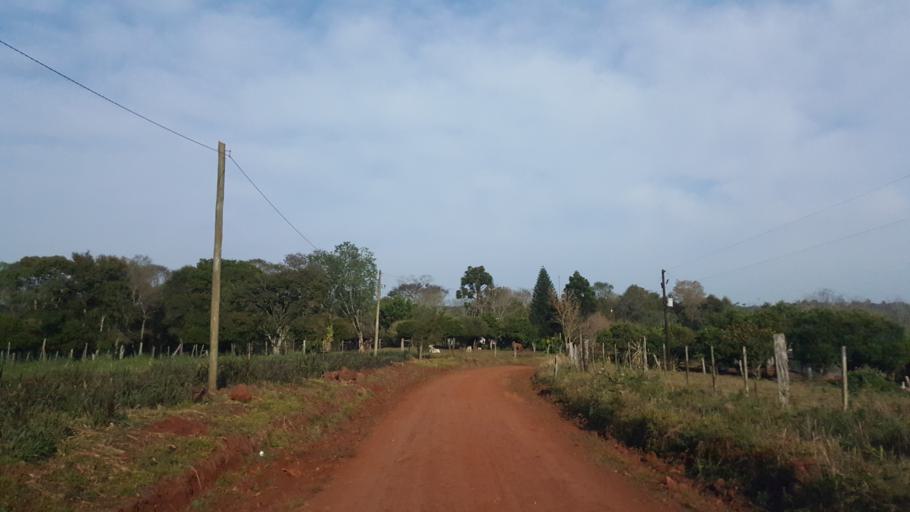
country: AR
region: Misiones
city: Capiovi
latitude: -26.9154
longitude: -55.0773
